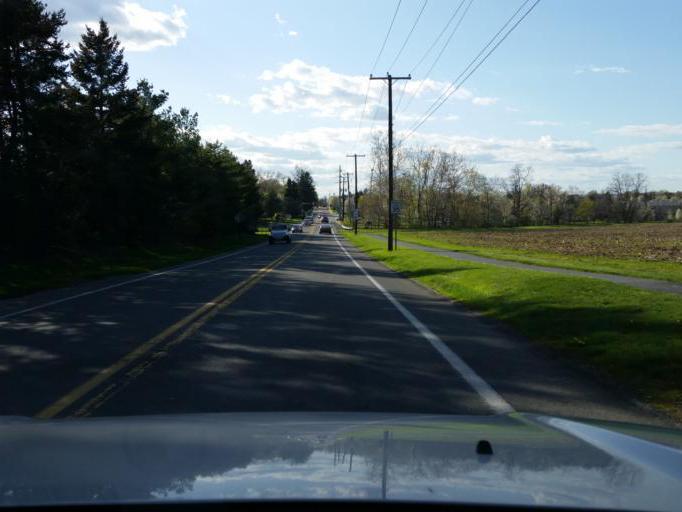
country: US
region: Pennsylvania
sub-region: Dauphin County
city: Hershey
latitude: 40.2660
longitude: -76.6452
